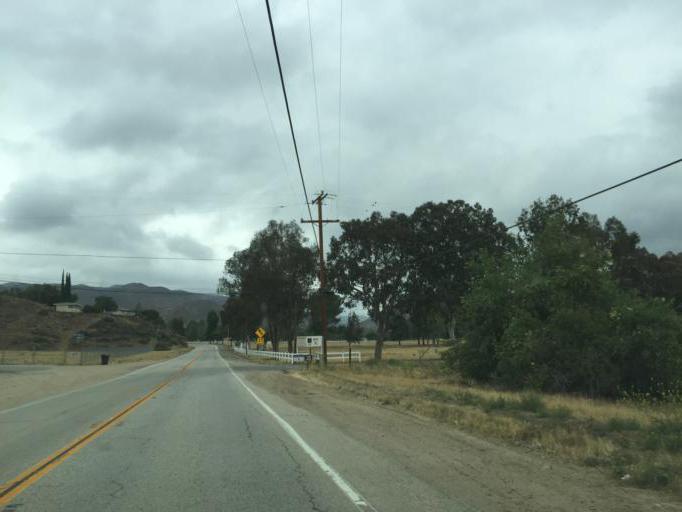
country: US
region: California
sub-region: Los Angeles County
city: Santa Clarita
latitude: 34.4771
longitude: -118.4660
